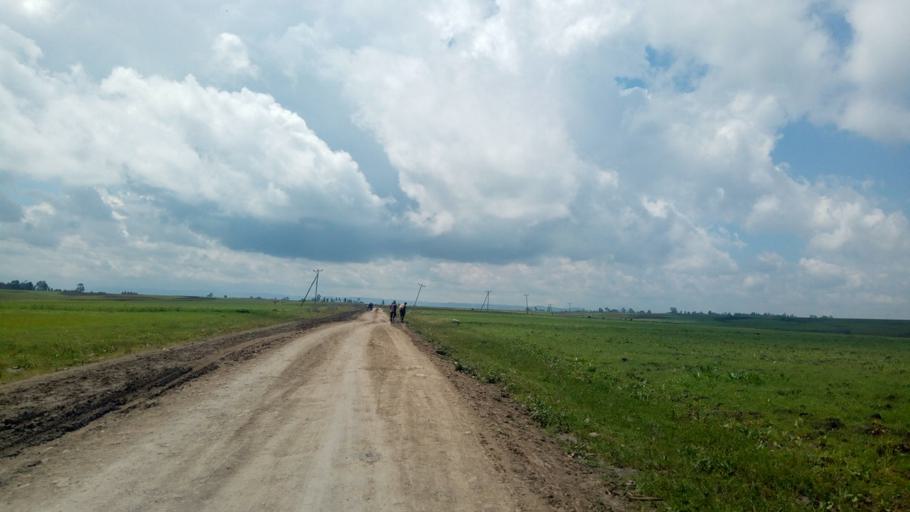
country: ET
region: Oromiya
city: Sendafa
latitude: 9.0021
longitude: 39.1262
